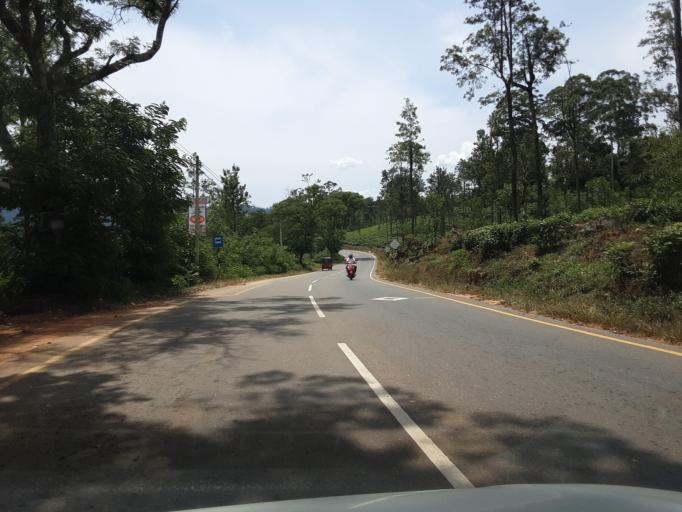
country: LK
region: Central
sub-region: Nuwara Eliya District
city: Nuwara Eliya
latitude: 6.9471
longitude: 80.9153
